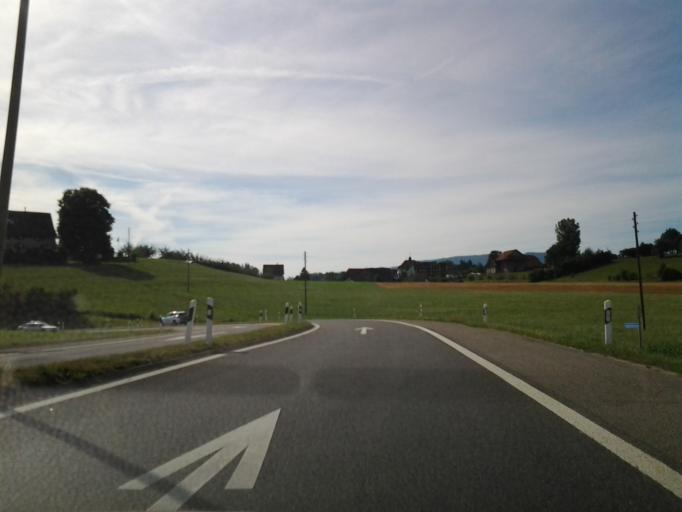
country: CH
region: Zurich
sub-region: Bezirk Horgen
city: Au
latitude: 47.2298
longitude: 8.6326
